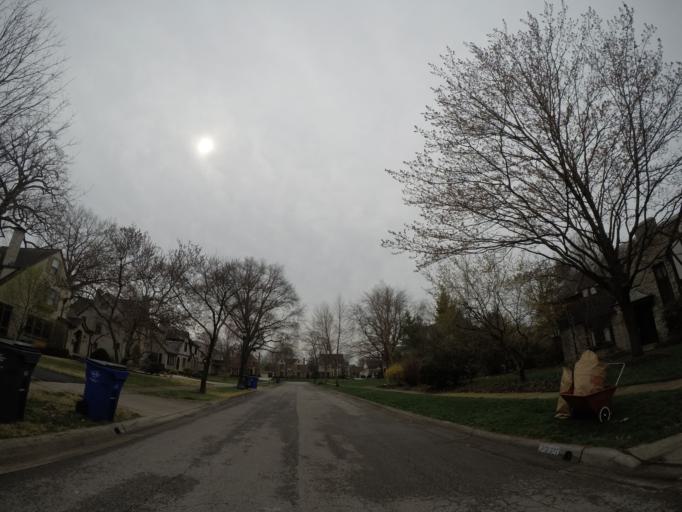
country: US
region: Ohio
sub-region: Franklin County
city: Upper Arlington
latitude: 40.0047
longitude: -83.0655
